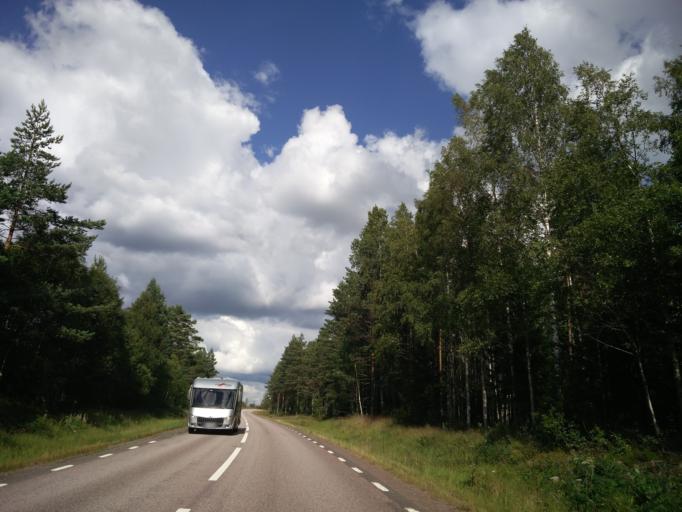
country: SE
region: Vaermland
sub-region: Sunne Kommun
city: Sunne
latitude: 59.6944
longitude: 13.0891
